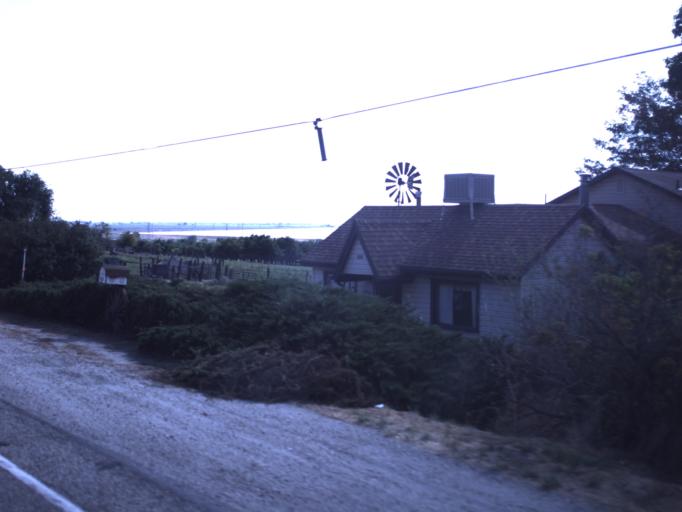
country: US
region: Utah
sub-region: Box Elder County
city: Willard
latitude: 41.3936
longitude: -112.0345
